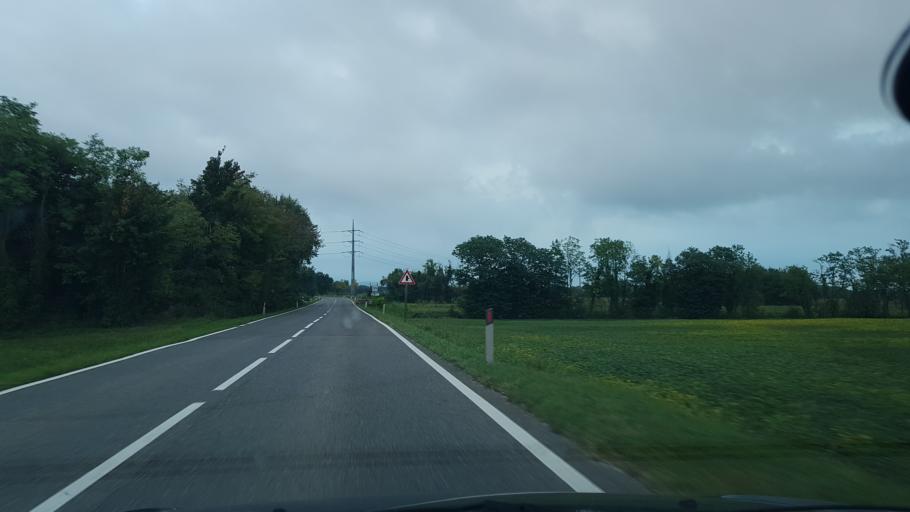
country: IT
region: Friuli Venezia Giulia
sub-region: Provincia di Udine
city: San Vito al Torre
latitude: 45.8920
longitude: 13.3868
